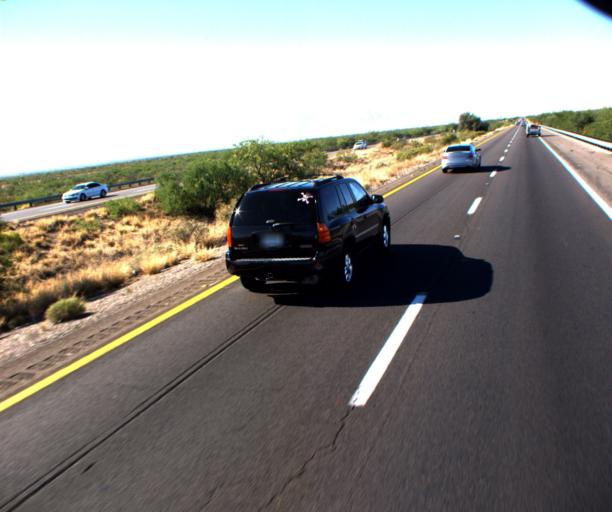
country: US
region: Arizona
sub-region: Pima County
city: Summit
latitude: 32.0502
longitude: -110.9930
